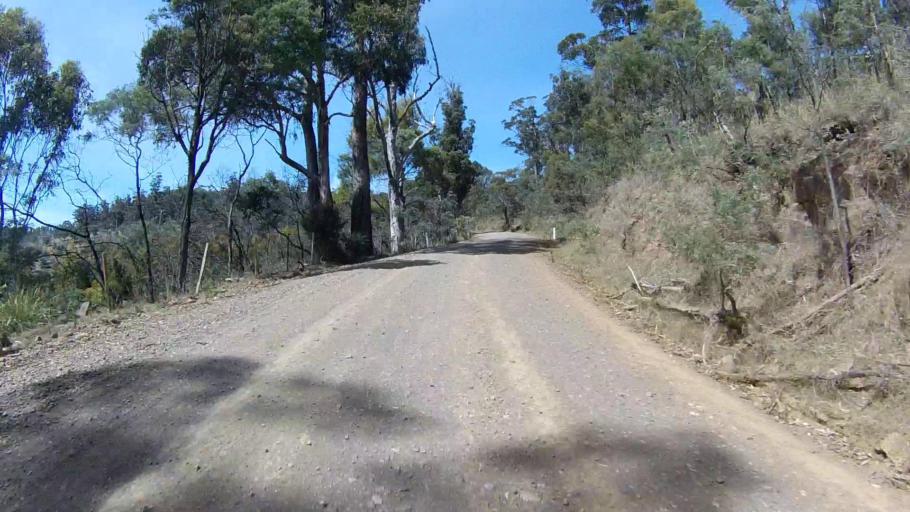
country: AU
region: Tasmania
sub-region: Sorell
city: Sorell
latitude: -42.6500
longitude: 147.7439
